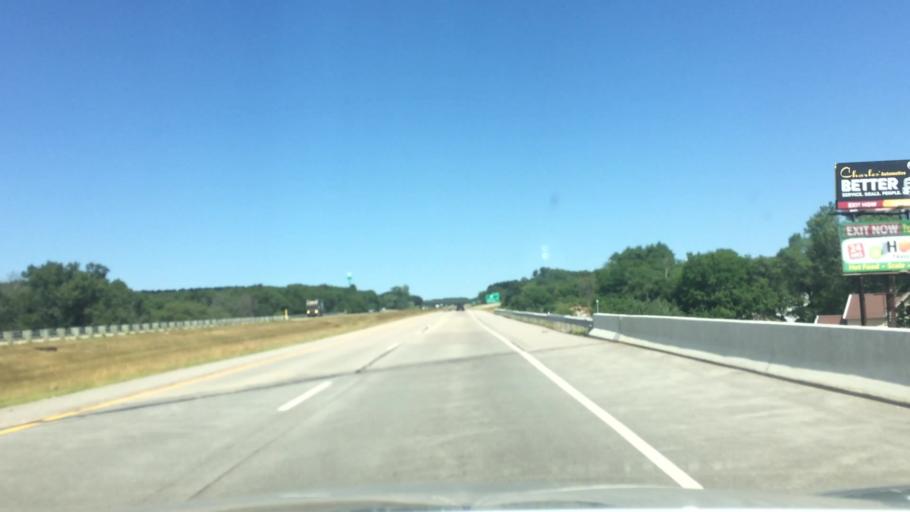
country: US
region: Wisconsin
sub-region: Marquette County
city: Westfield
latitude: 44.0282
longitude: -89.5221
